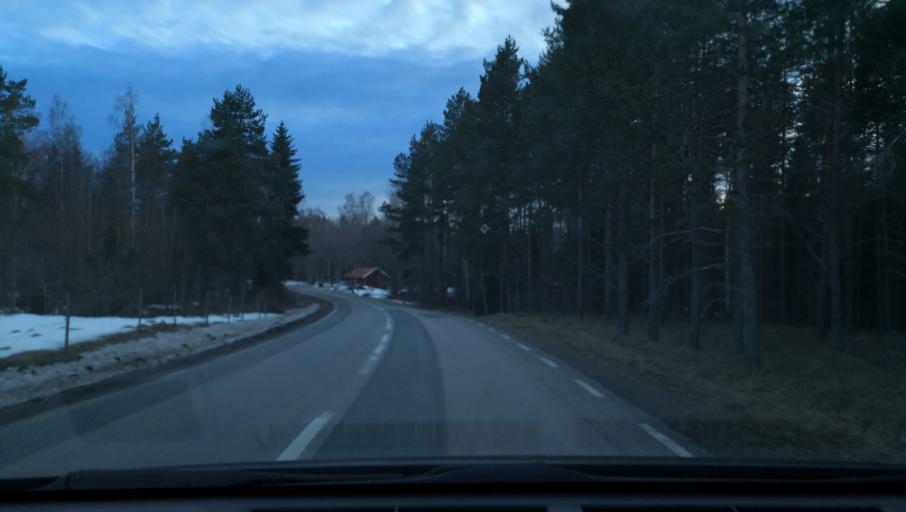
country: SE
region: Uppsala
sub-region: Osthammars Kommun
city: Osterbybruk
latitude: 60.2774
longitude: 17.9624
